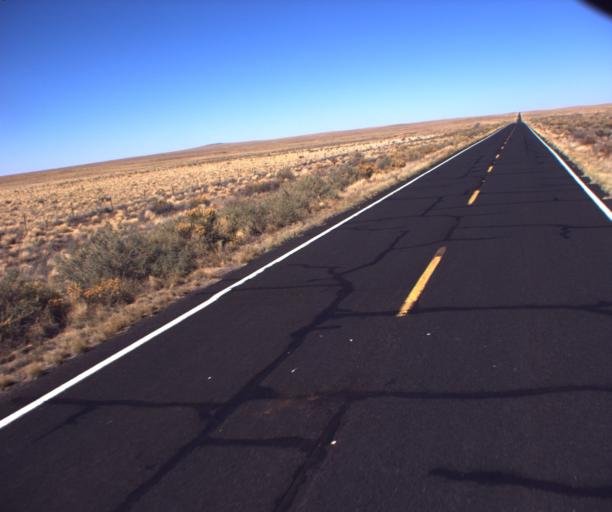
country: US
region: Arizona
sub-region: Navajo County
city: Dilkon
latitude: 35.5826
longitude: -110.4645
